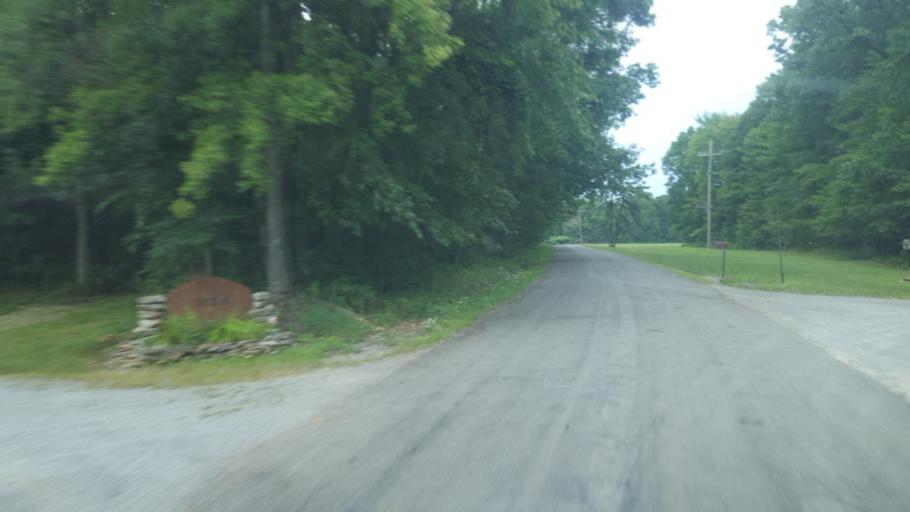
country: US
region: Pennsylvania
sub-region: Clarion County
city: Marianne
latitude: 41.2149
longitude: -79.4227
